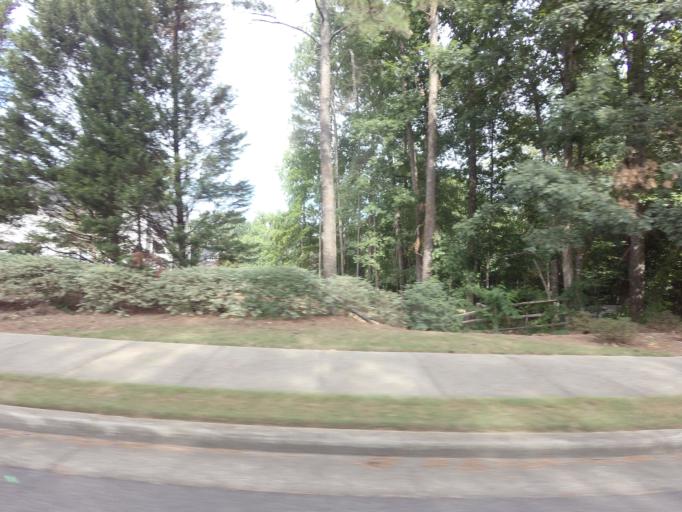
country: US
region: Georgia
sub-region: Gwinnett County
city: Duluth
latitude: 34.0510
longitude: -84.1442
